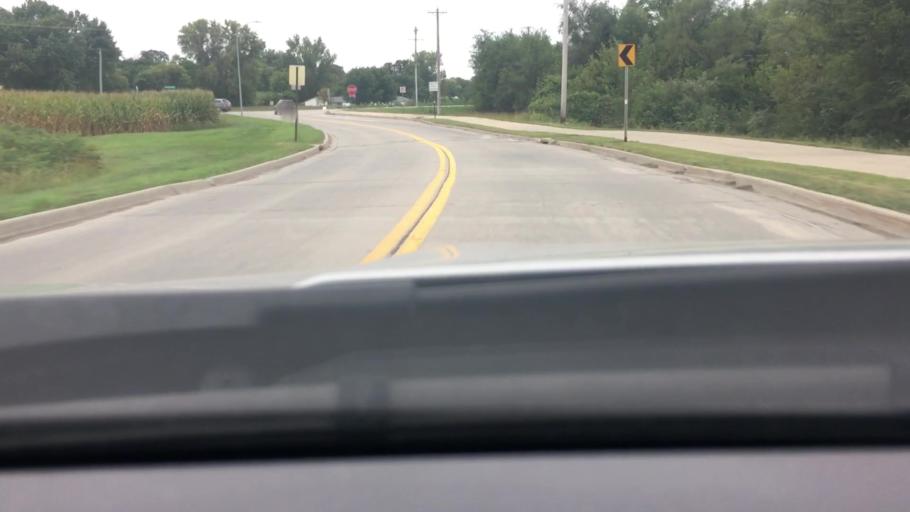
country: US
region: Iowa
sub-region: Pottawattamie County
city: Council Bluffs
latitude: 41.2617
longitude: -95.8053
